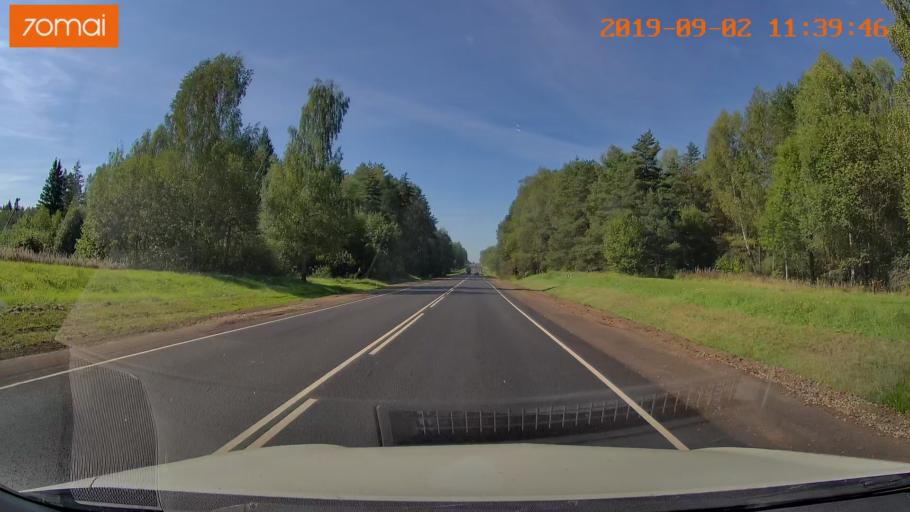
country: RU
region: Smolensk
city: Oster
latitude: 53.9060
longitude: 32.7164
